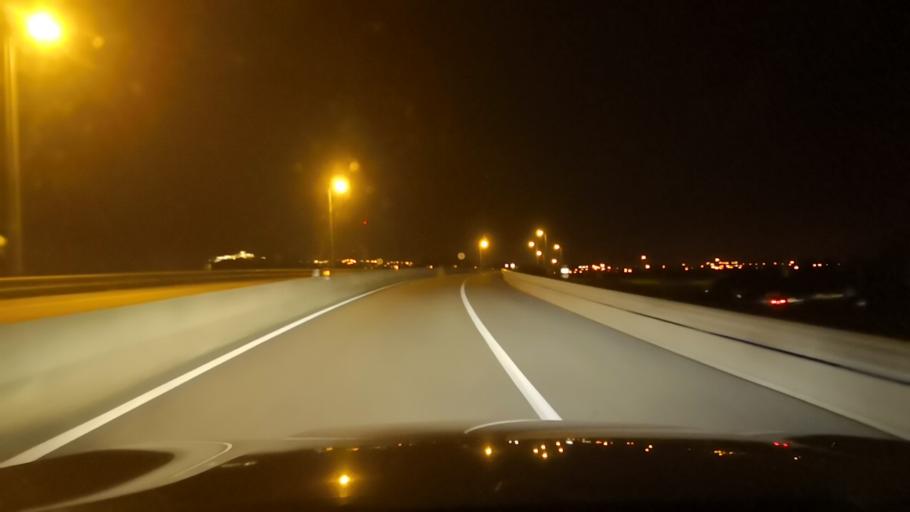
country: PT
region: Setubal
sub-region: Setubal
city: Setubal
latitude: 38.5541
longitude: -8.8670
